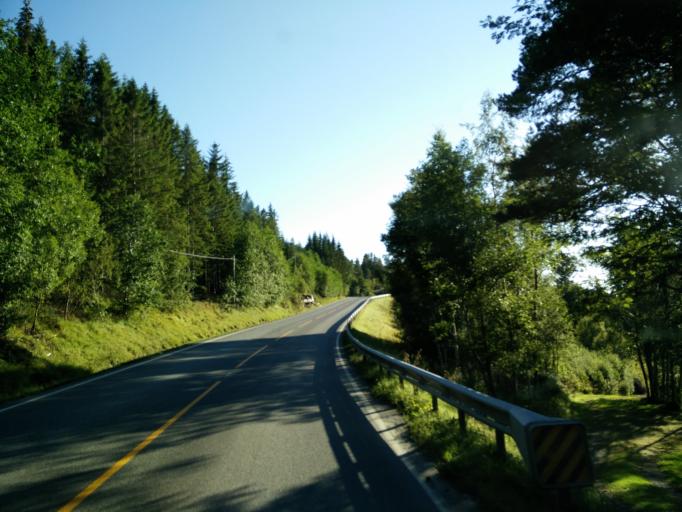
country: NO
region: More og Romsdal
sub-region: Halsa
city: Liaboen
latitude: 63.0829
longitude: 8.3414
